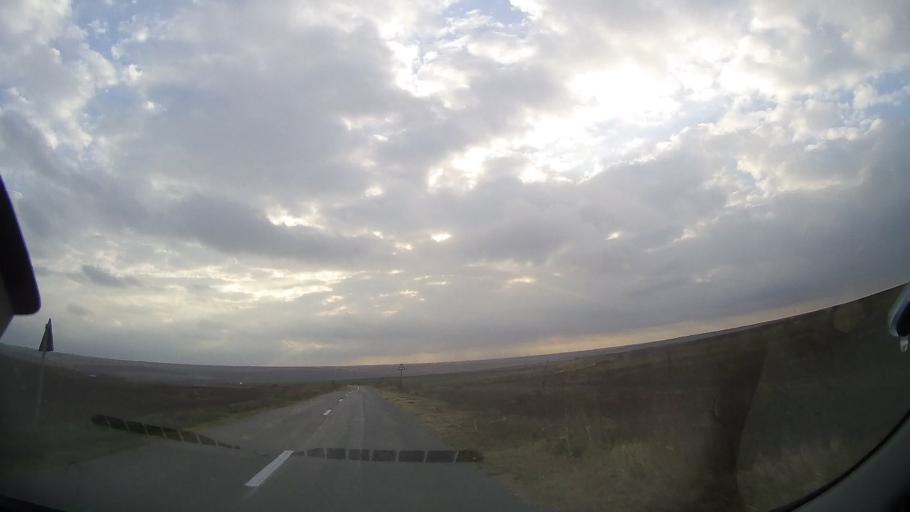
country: RO
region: Constanta
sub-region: Comuna Deleni
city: Pietreni
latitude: 44.1251
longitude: 28.1072
